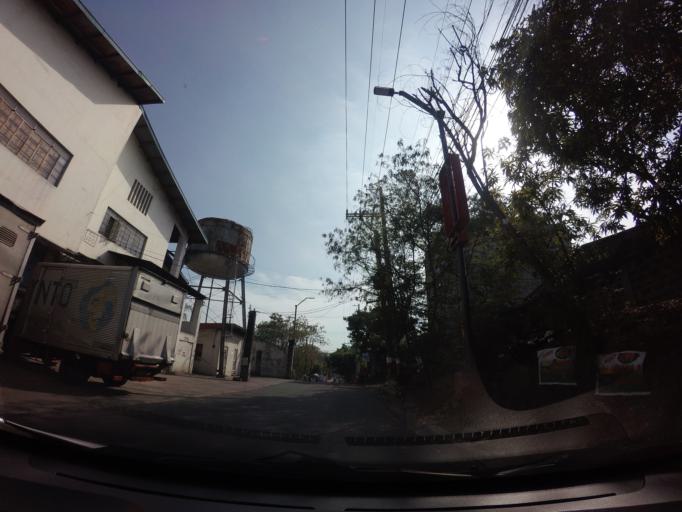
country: PH
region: Calabarzon
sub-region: Province of Rizal
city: Taguig
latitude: 14.5154
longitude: 121.0499
